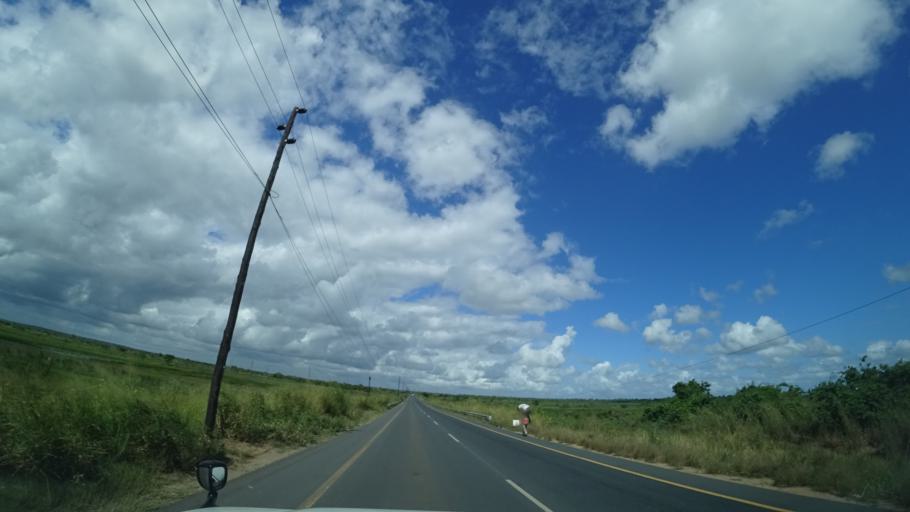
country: MZ
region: Sofala
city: Dondo
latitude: -19.5096
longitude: 34.6104
